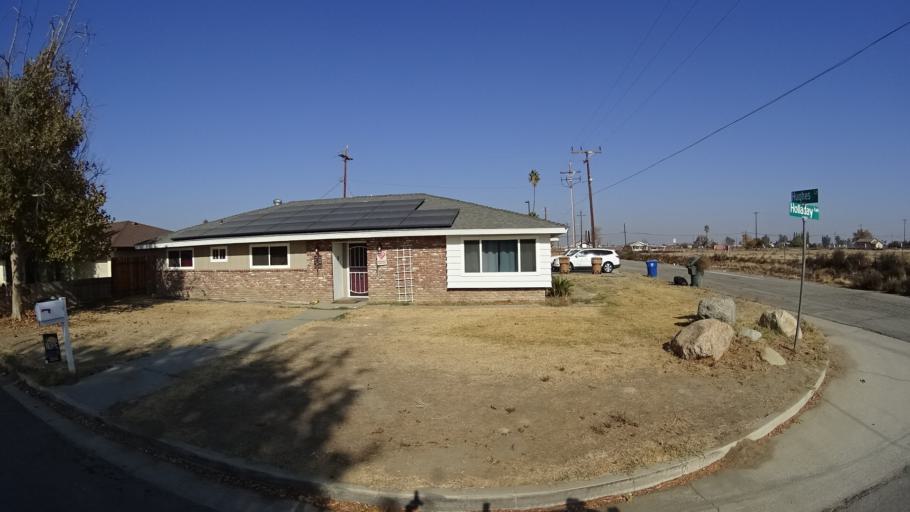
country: US
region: California
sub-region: Kern County
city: Greenfield
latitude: 35.2656
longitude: -119.0304
